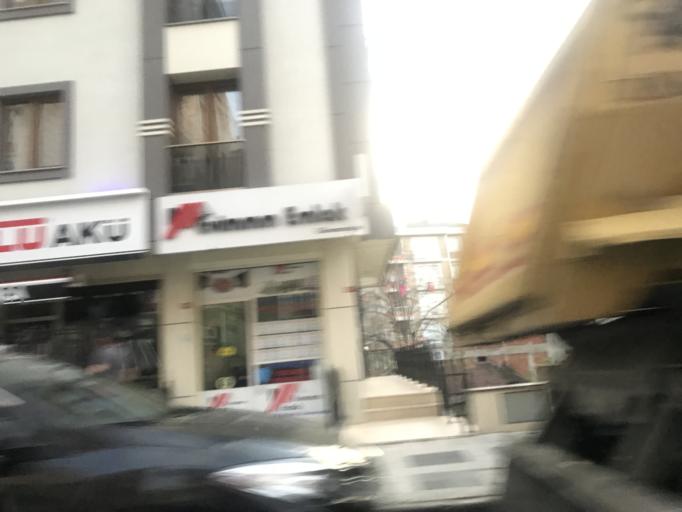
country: TR
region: Istanbul
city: Umraniye
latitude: 41.0360
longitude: 29.1017
